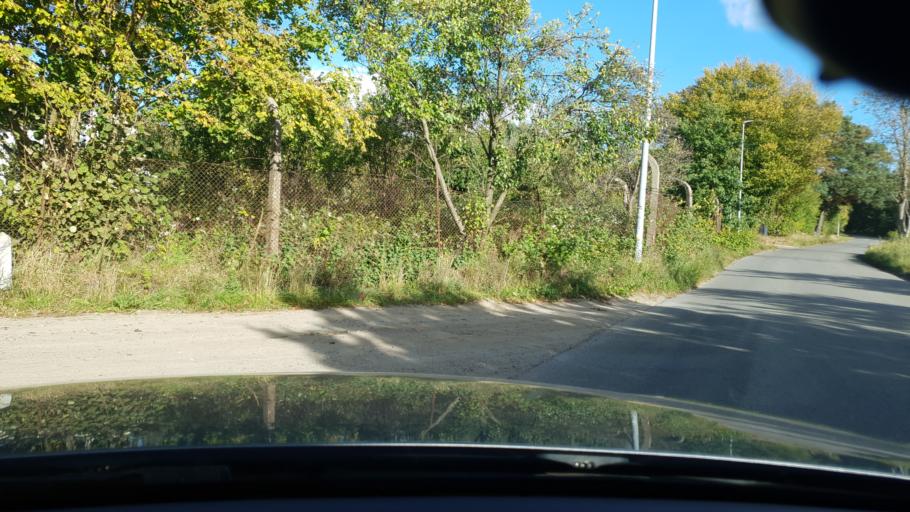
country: PL
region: Pomeranian Voivodeship
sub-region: Powiat kartuski
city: Chwaszczyno
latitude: 54.4821
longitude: 18.4271
